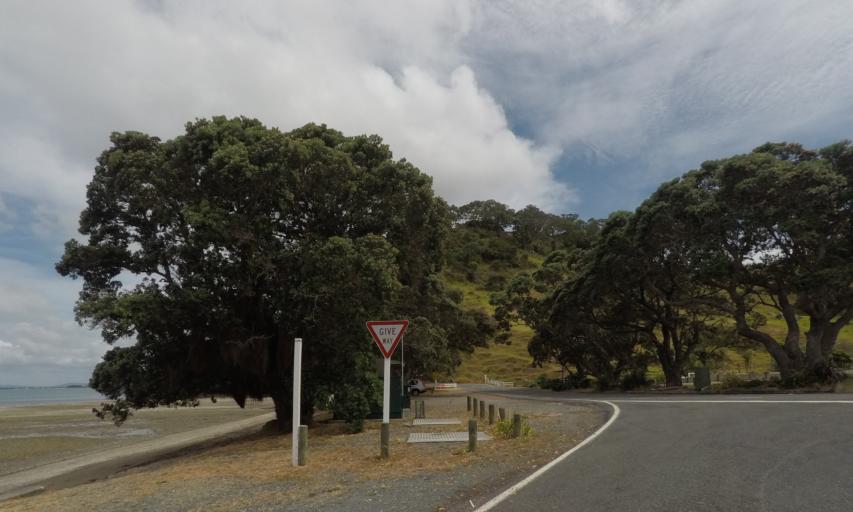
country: NZ
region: Northland
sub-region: Whangarei
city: Ruakaka
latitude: -35.8407
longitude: 174.5358
